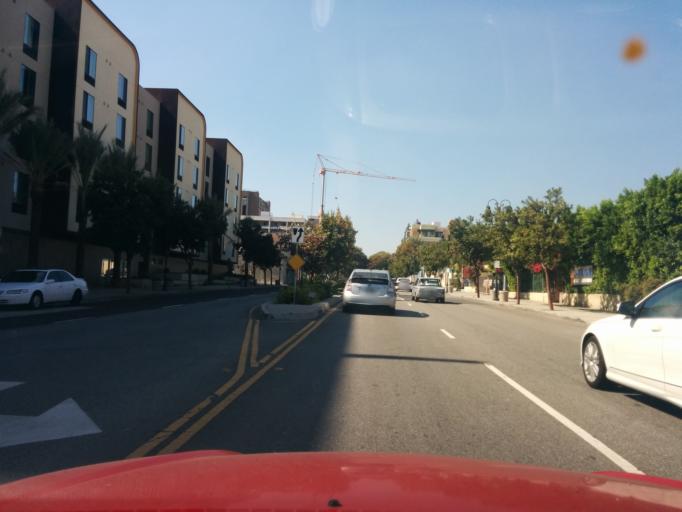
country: US
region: California
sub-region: Los Angeles County
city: Burbank
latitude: 34.1774
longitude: -118.3039
